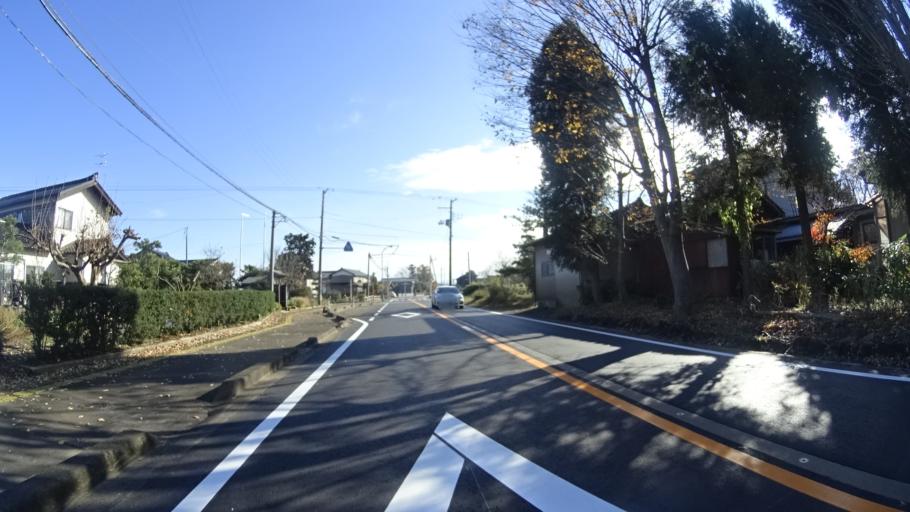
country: JP
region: Niigata
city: Mitsuke
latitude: 37.5547
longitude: 138.8546
